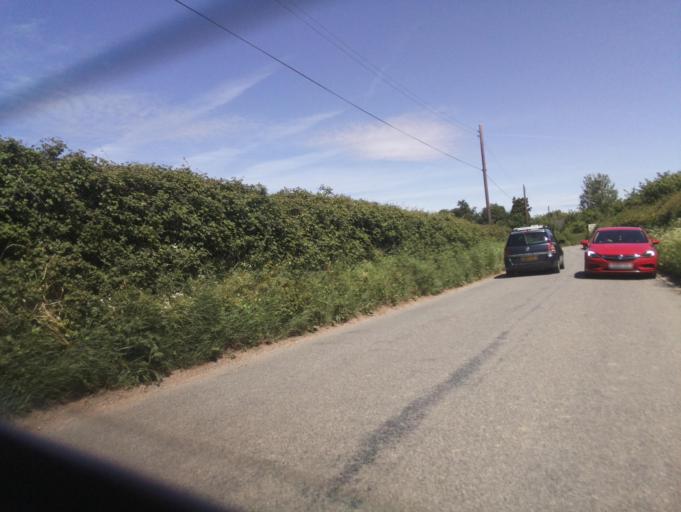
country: GB
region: England
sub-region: Devon
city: Ottery St Mary
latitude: 50.7701
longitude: -3.2618
